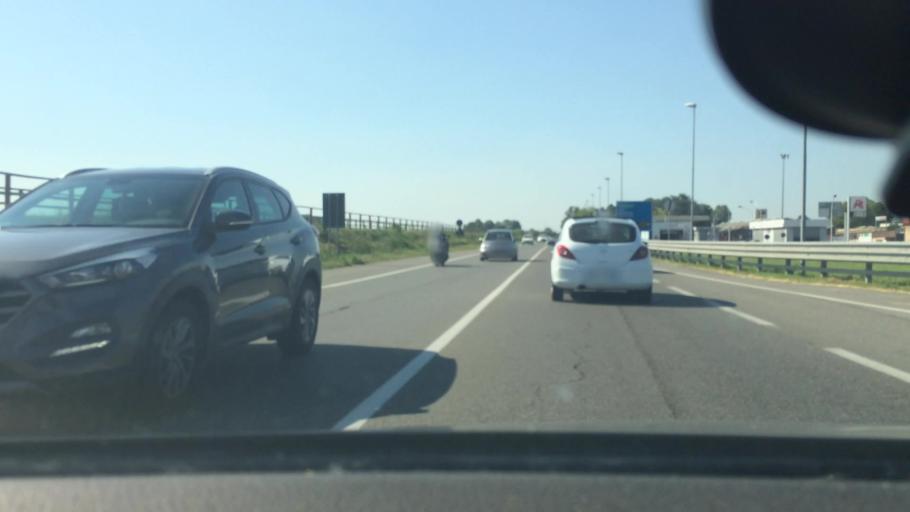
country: IT
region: Lombardy
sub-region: Provincia di Lodi
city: San Rocco al Porto
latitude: 45.0711
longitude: 9.7092
